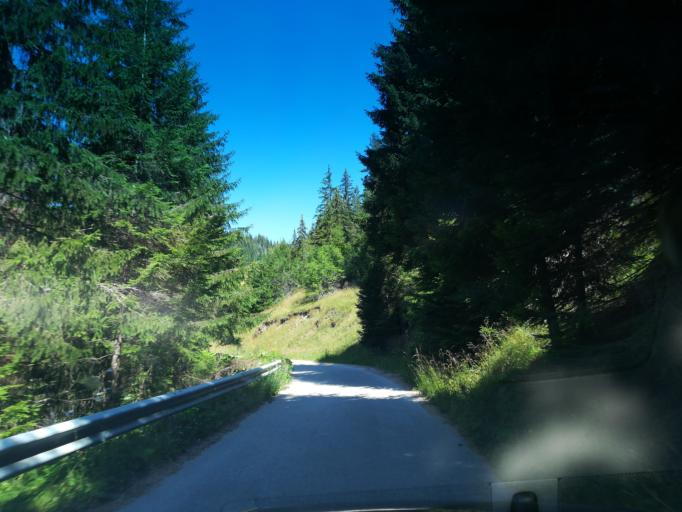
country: BG
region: Smolyan
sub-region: Obshtina Chepelare
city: Chepelare
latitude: 41.6719
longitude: 24.7924
